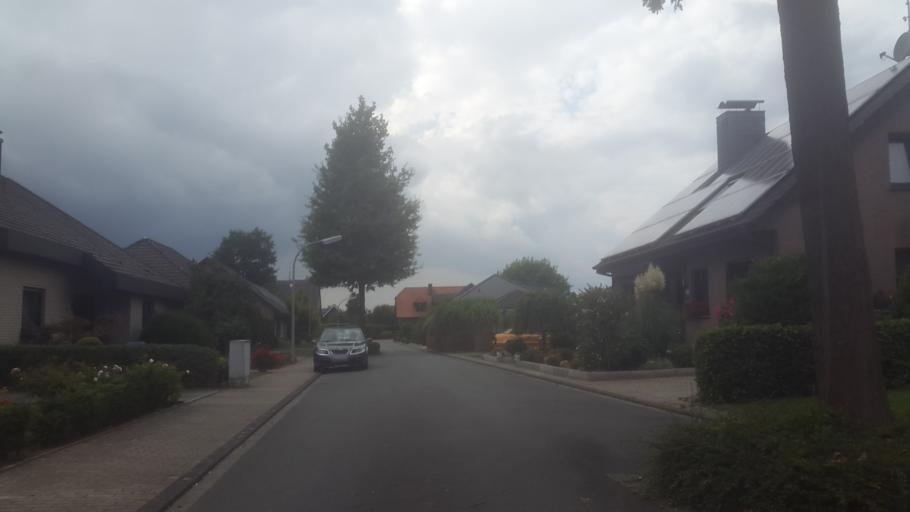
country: DE
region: North Rhine-Westphalia
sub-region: Regierungsbezirk Munster
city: Everswinkel
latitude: 51.9764
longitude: 7.9024
